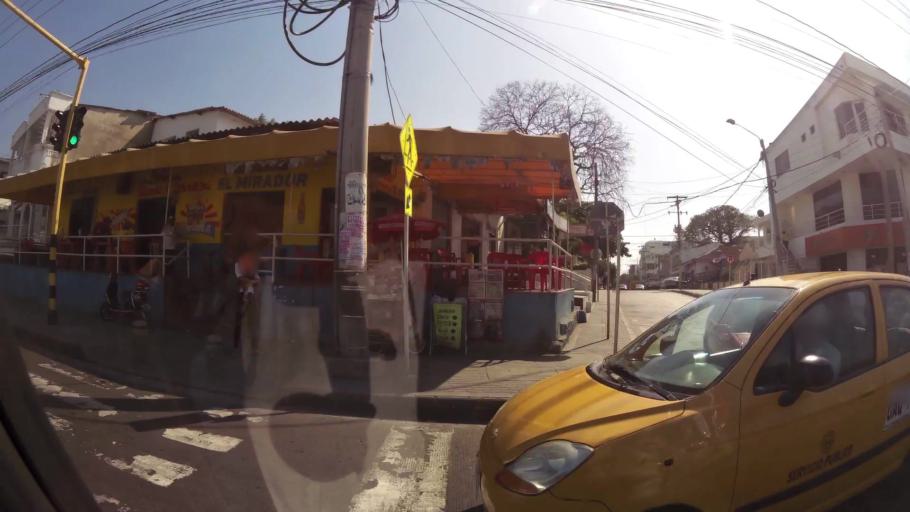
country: CO
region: Bolivar
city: Cartagena
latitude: 10.4081
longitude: -75.5125
